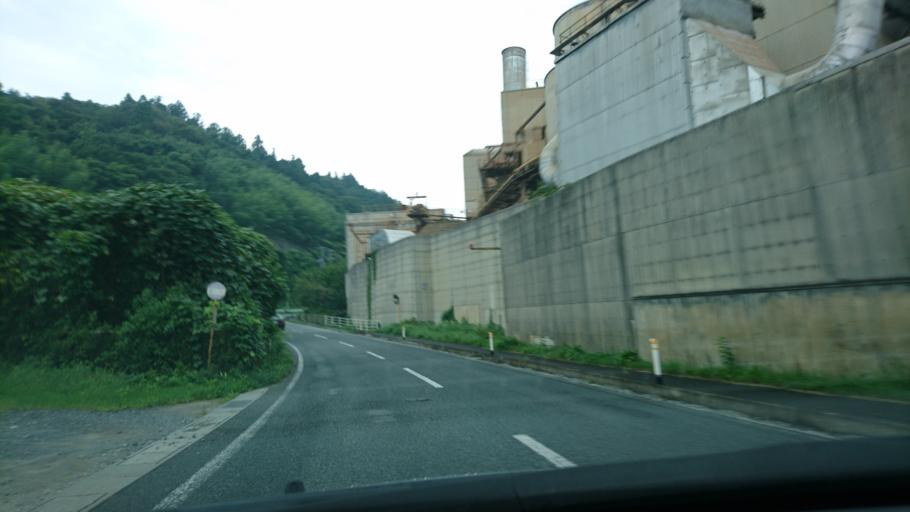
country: JP
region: Iwate
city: Ichinoseki
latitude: 38.9835
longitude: 141.2437
